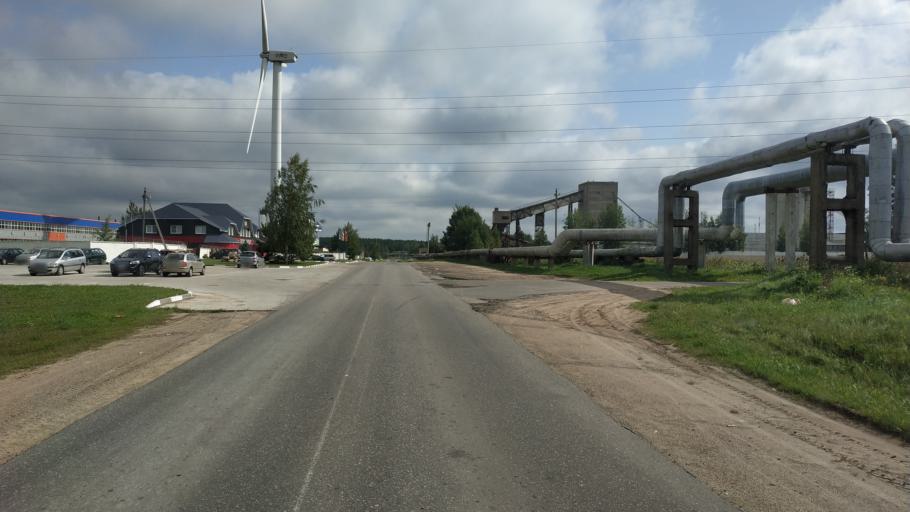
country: BY
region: Mogilev
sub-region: Mahilyowski Rayon
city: Veyno
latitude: 53.8400
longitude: 30.3767
